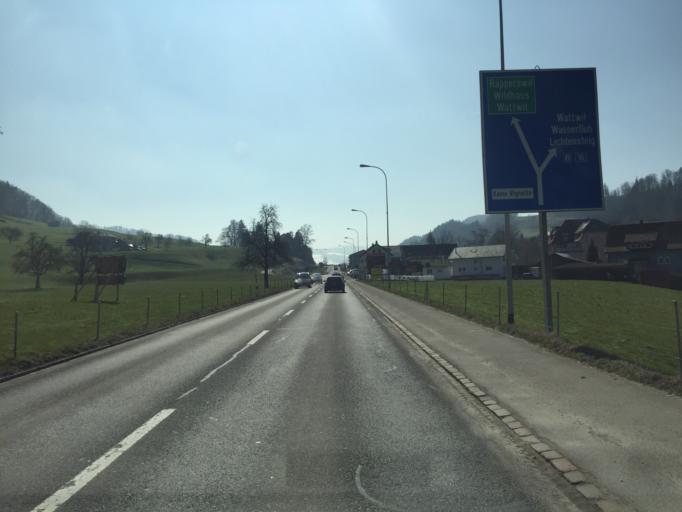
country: CH
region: Saint Gallen
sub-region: Wahlkreis Toggenburg
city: Buetschwil
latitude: 47.3449
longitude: 9.0818
